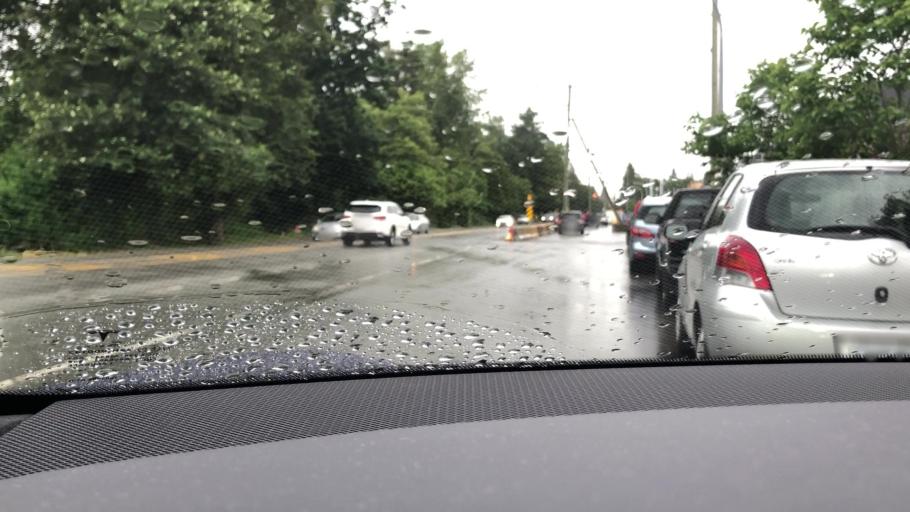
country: CA
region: British Columbia
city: Walnut Grove
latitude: 49.1328
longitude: -122.6455
